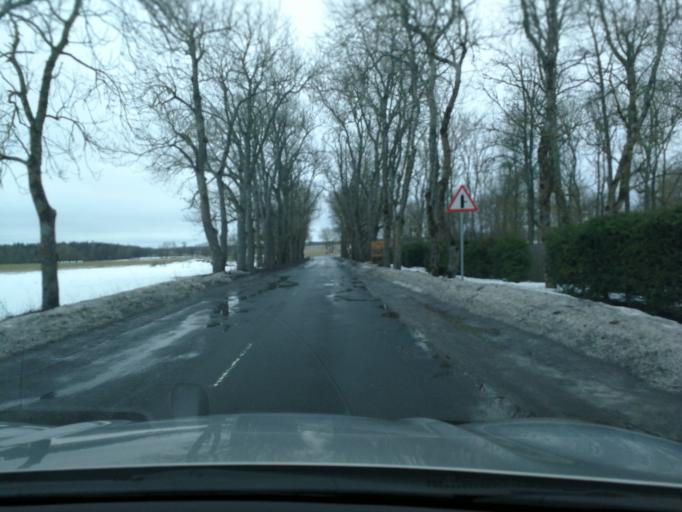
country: EE
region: Harju
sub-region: Kiili vald
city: Kiili
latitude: 59.2747
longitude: 24.8748
